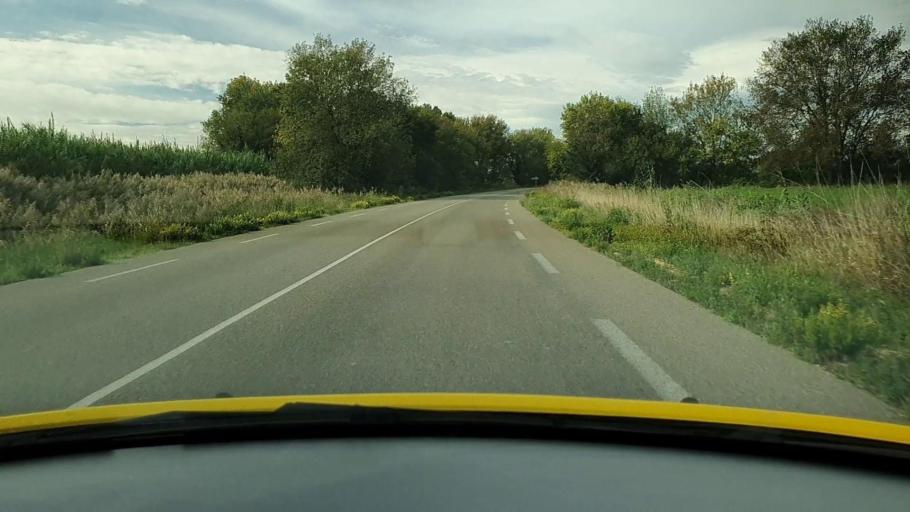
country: FR
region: Languedoc-Roussillon
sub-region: Departement du Gard
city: Bellegarde
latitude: 43.7482
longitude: 4.5262
